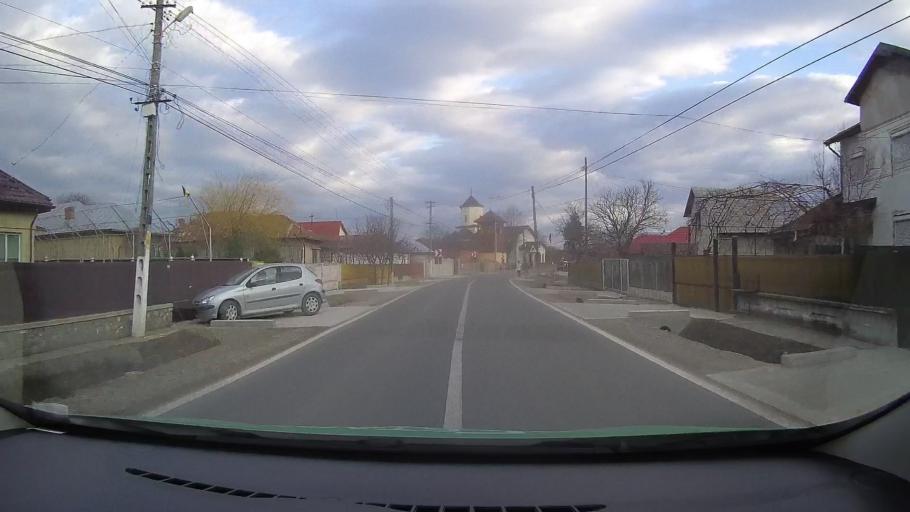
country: RO
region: Dambovita
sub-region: Comuna I. L. Caragiale
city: Ghirdoveni
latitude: 44.9345
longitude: 25.6845
